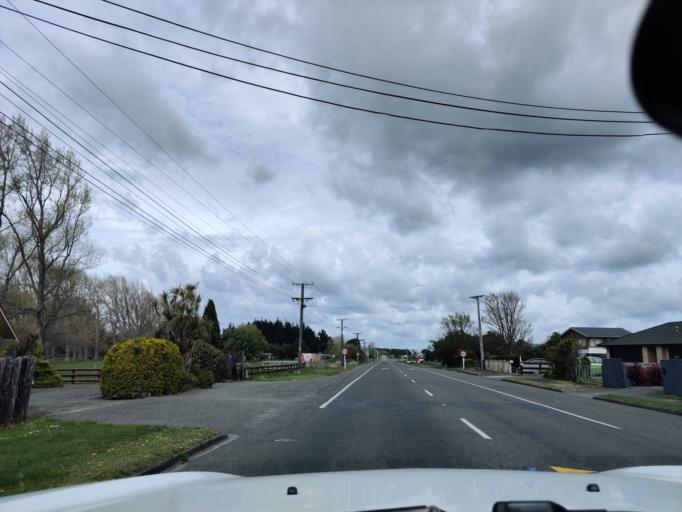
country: NZ
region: Manawatu-Wanganui
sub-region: Palmerston North City
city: Palmerston North
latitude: -40.2350
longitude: 175.5523
